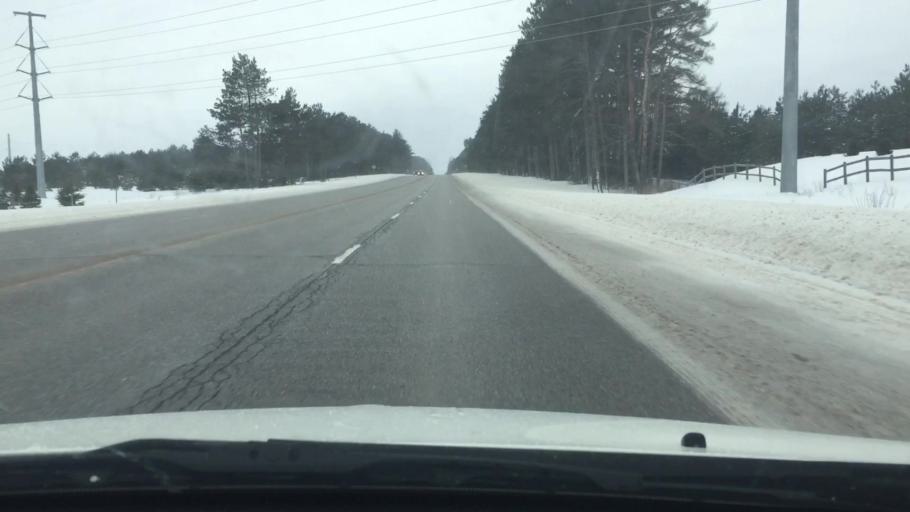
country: US
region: Michigan
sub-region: Otsego County
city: Gaylord
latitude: 45.0621
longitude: -84.8294
